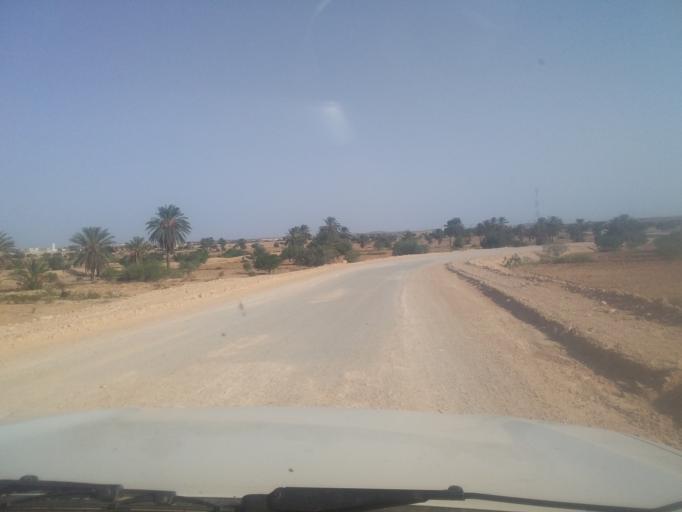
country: TN
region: Qabis
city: Matmata
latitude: 33.5804
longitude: 10.2629
